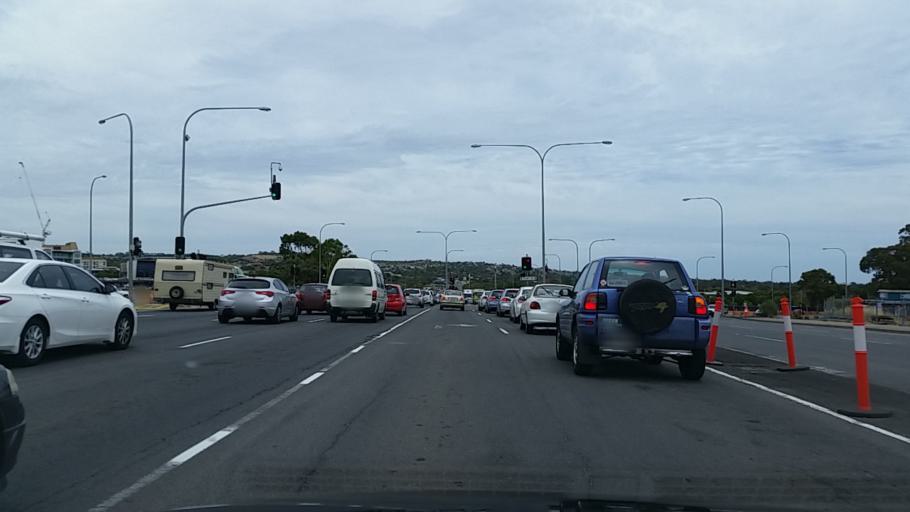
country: AU
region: South Australia
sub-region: Marion
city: Marion
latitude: -35.0160
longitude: 138.5704
